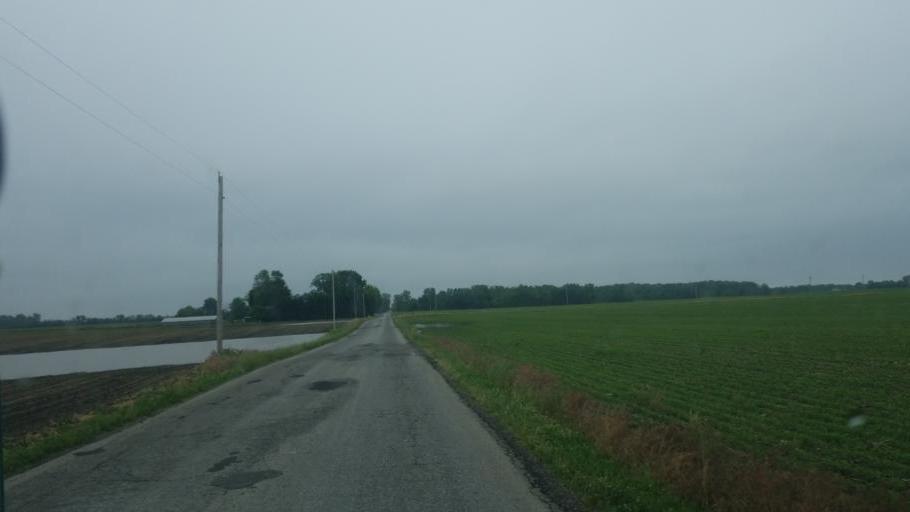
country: US
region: Indiana
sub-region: Marshall County
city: Bremen
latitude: 41.4708
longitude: -86.1177
